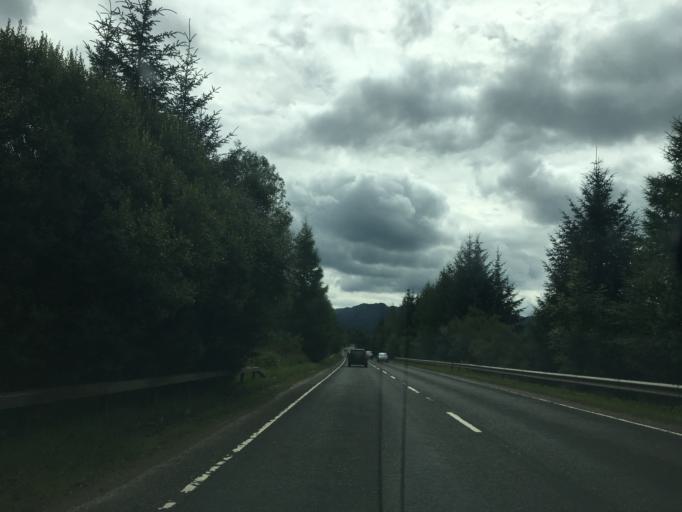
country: GB
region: Scotland
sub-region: Stirling
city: Callander
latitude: 56.3481
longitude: -4.3280
